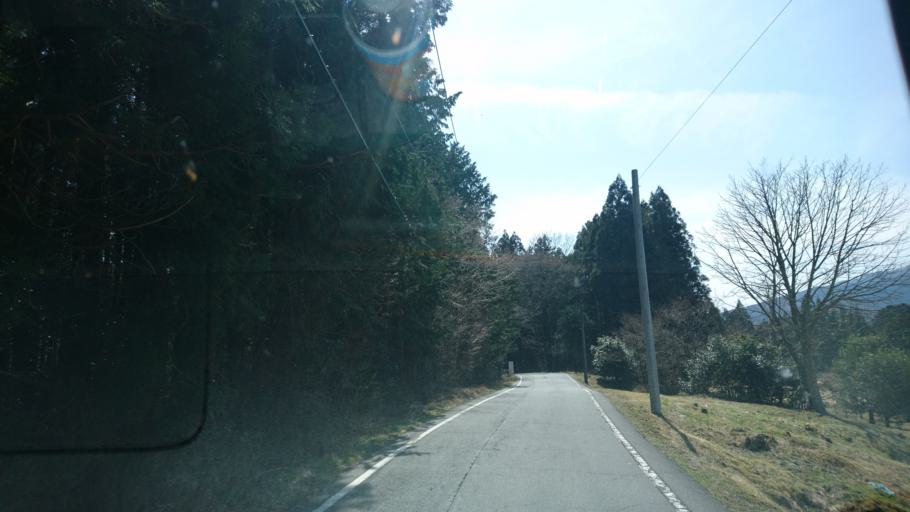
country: JP
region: Shizuoka
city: Fujinomiya
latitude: 35.3571
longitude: 138.5708
